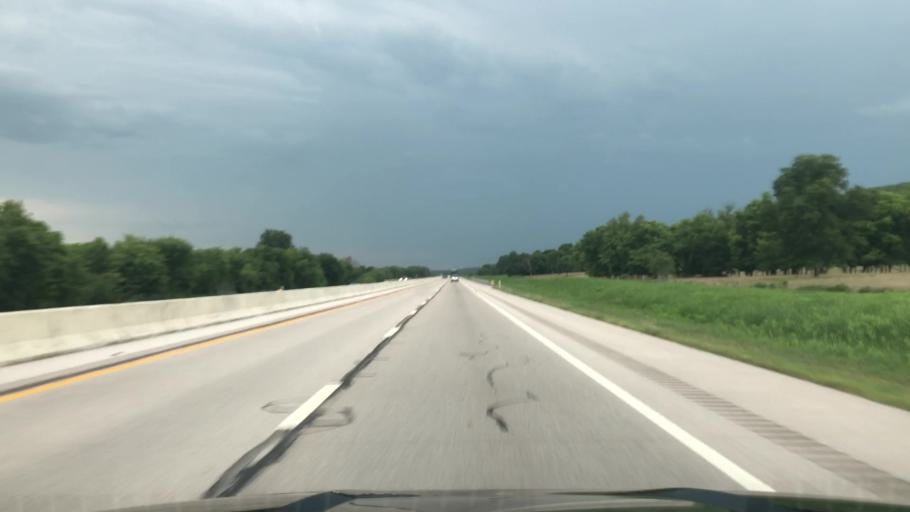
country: US
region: Oklahoma
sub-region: Rogers County
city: Bushyhead
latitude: 36.3650
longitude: -95.4491
